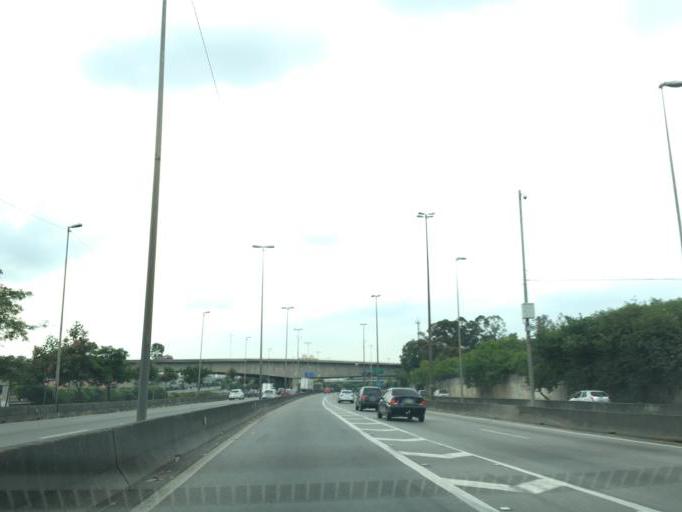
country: BR
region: Sao Paulo
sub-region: Osasco
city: Osasco
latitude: -23.5225
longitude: -46.7473
